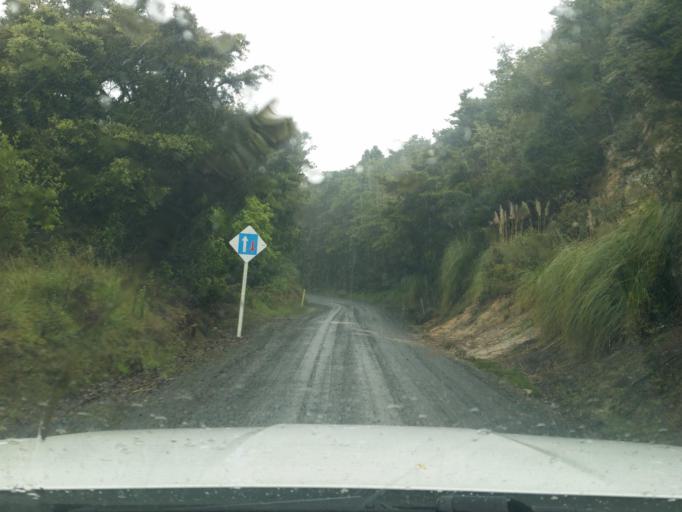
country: NZ
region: Northland
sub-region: Kaipara District
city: Dargaville
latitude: -35.7628
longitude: 173.9659
